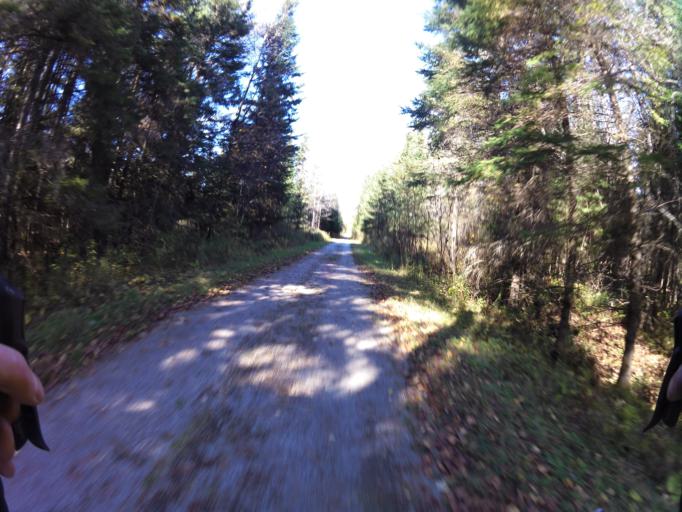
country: CA
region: Quebec
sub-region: Outaouais
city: Wakefield
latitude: 45.8857
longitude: -76.0316
